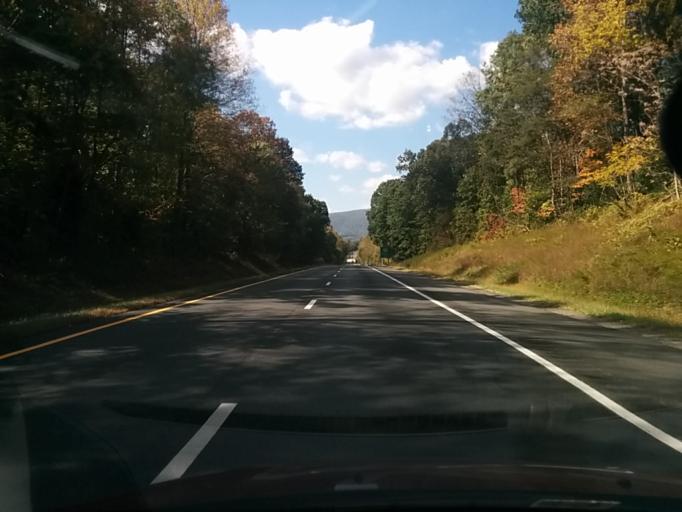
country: US
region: Virginia
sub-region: Albemarle County
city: Crozet
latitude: 38.0374
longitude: -78.7022
